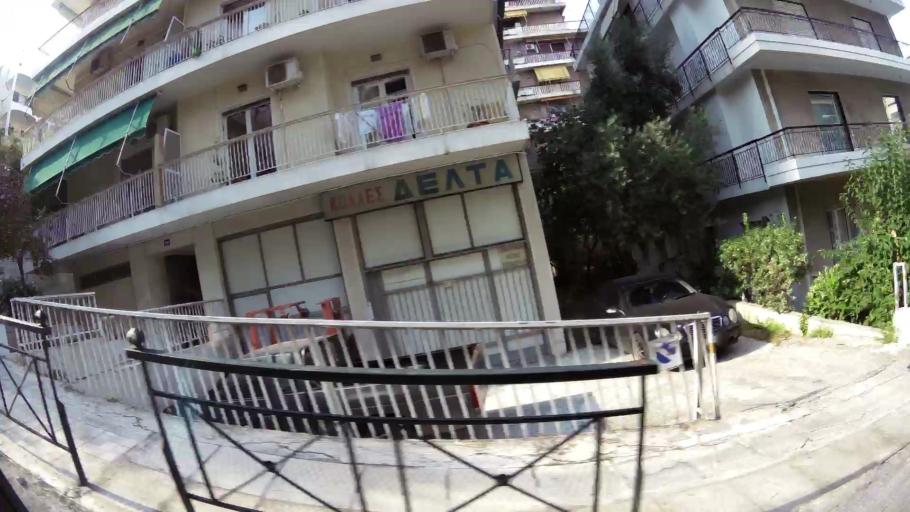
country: GR
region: Attica
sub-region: Nomarchia Athinas
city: Galatsi
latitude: 38.0098
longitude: 23.7489
